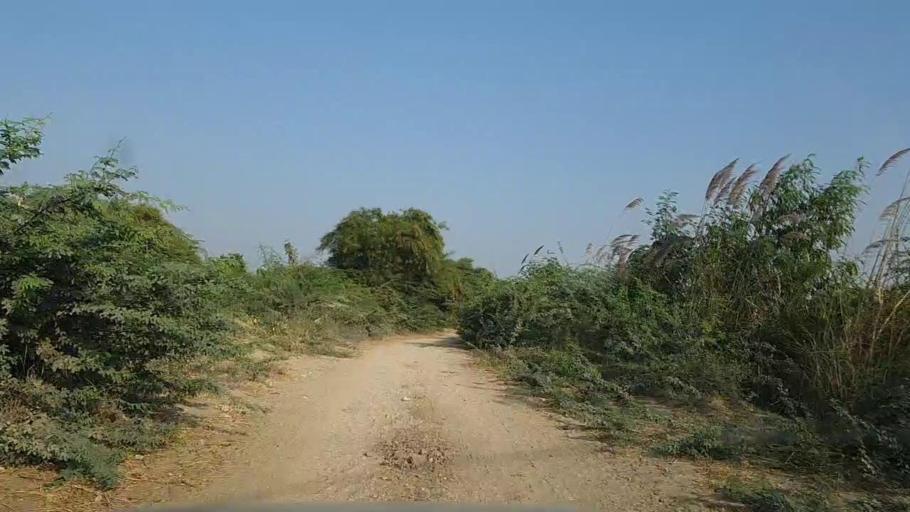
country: PK
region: Sindh
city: Mirpur Sakro
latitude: 24.5999
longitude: 67.6501
